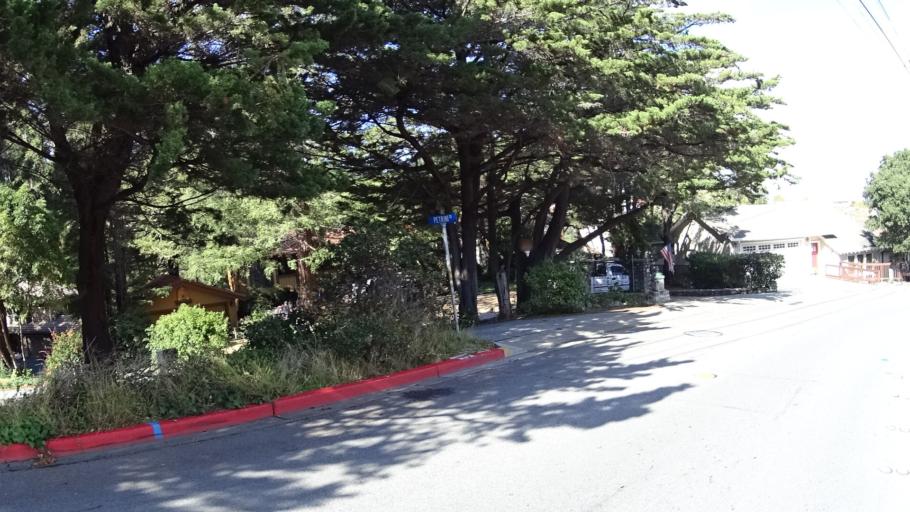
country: US
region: California
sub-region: San Mateo County
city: Millbrae
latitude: 37.5922
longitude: -122.4018
